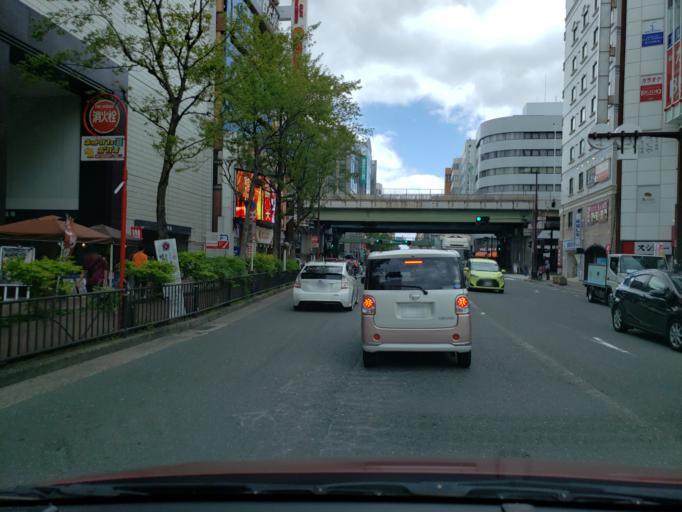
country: JP
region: Osaka
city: Suita
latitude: 34.7576
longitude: 135.4961
